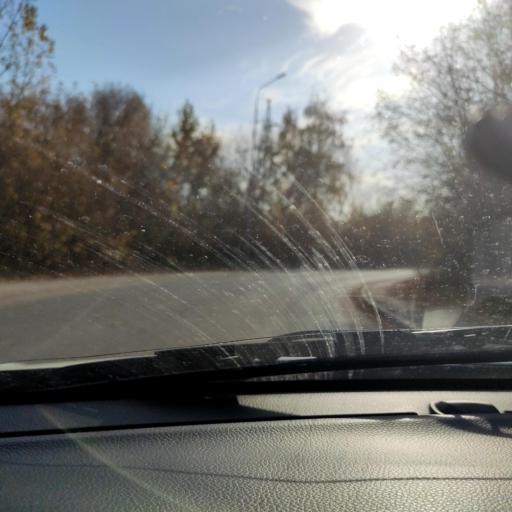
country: RU
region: Tatarstan
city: Verkhniy Uslon
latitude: 55.8036
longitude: 49.0477
